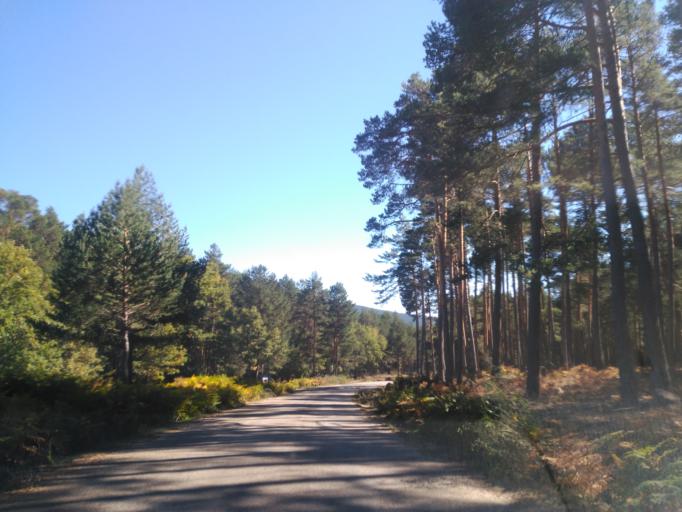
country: ES
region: Castille and Leon
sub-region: Provincia de Soria
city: Vinuesa
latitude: 41.9622
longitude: -2.7875
